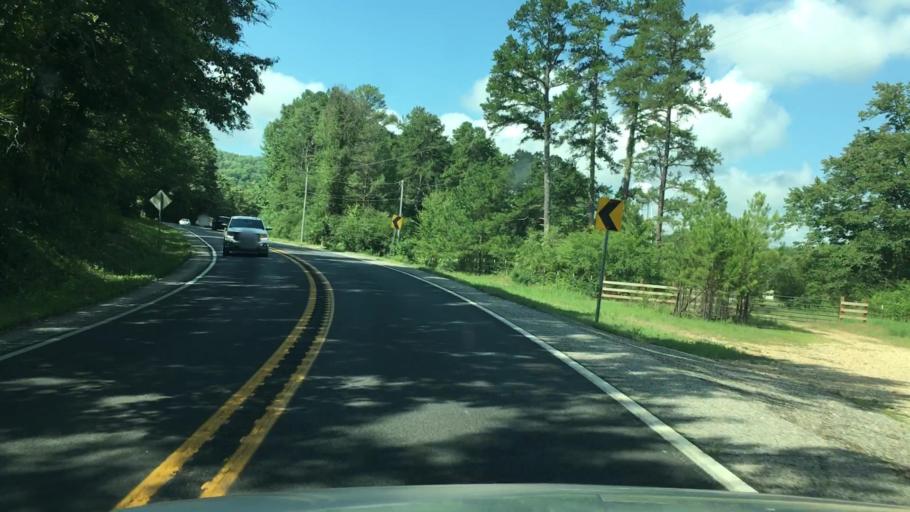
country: US
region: Arkansas
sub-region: Garland County
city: Lake Hamilton
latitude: 34.3827
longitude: -93.1340
